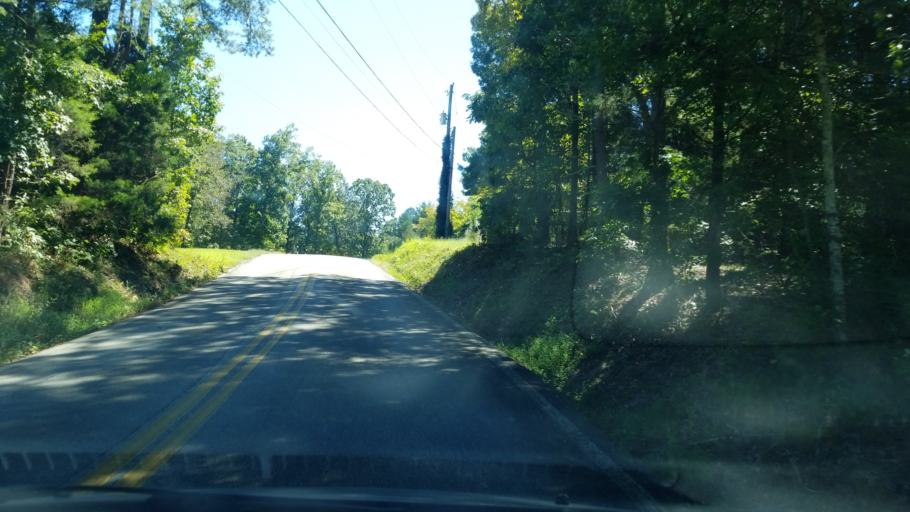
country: US
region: Tennessee
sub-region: Hamilton County
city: Collegedale
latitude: 35.0972
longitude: -85.0839
